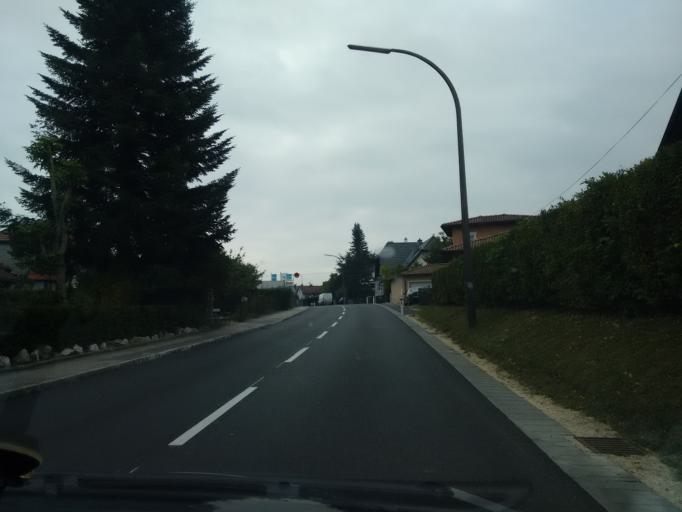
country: AT
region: Upper Austria
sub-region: Politischer Bezirk Steyr-Land
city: Bad Hall
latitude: 48.0268
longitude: 14.2217
